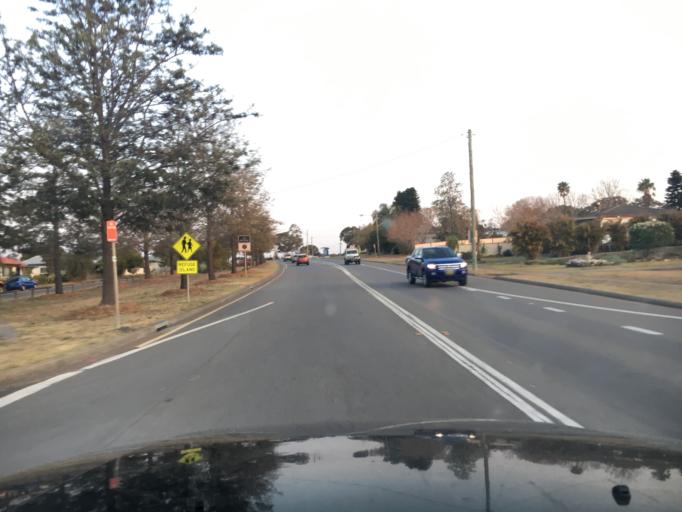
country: AU
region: New South Wales
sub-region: Cessnock
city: Greta
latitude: -32.6807
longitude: 151.3915
